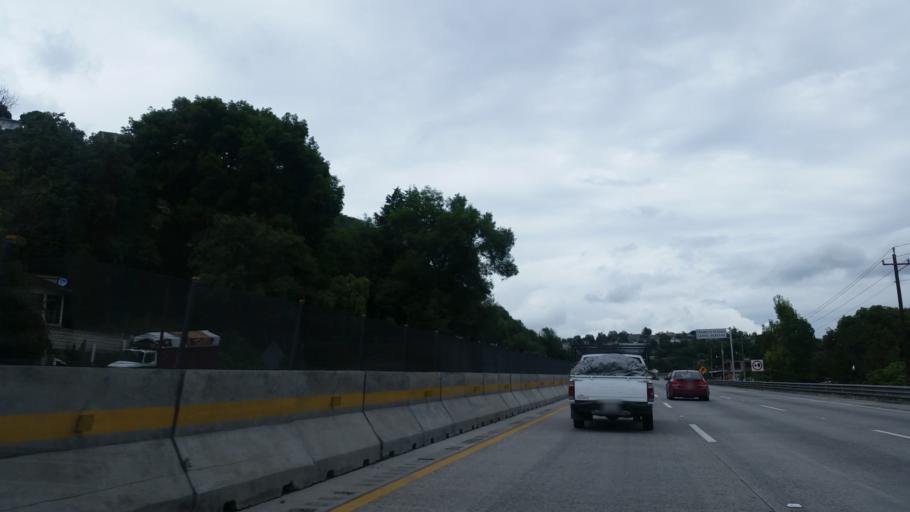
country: MX
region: Hidalgo
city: Tepeji de Ocampo
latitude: 19.8967
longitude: -99.3485
